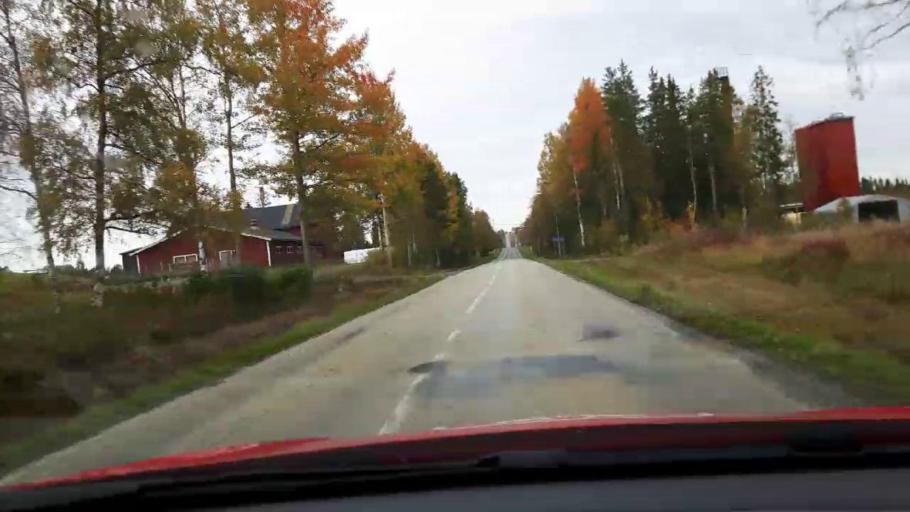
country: SE
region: Jaemtland
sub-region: Bergs Kommun
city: Hoverberg
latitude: 62.9933
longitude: 14.3394
